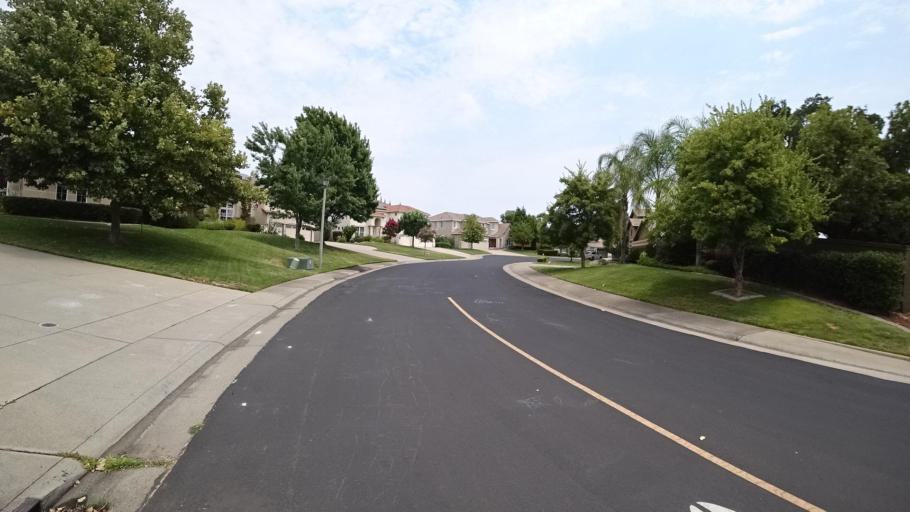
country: US
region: California
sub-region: Placer County
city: Rocklin
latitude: 38.7769
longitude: -121.2174
